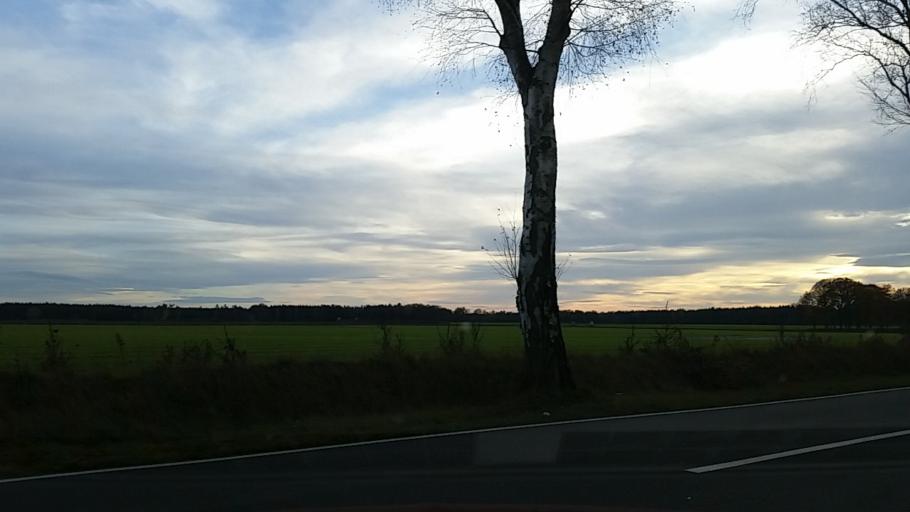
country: DE
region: Lower Saxony
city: Sprakensehl
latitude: 52.7928
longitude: 10.5109
